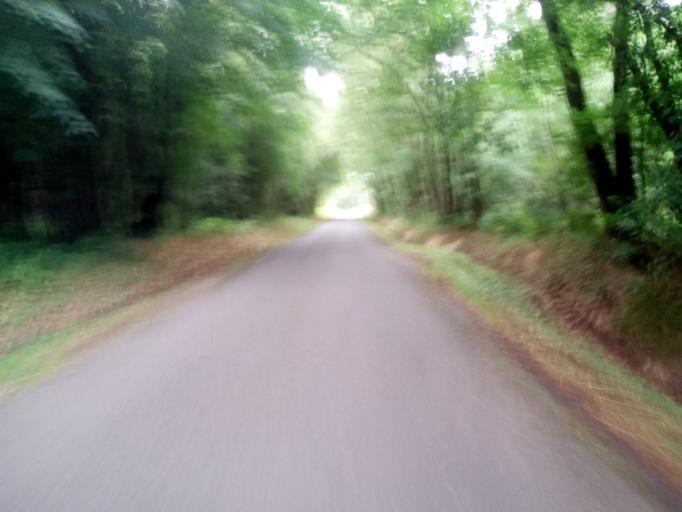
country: FR
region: Lower Normandy
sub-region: Departement du Calvados
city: Clinchamps-sur-Orne
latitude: 49.0251
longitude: -0.3965
